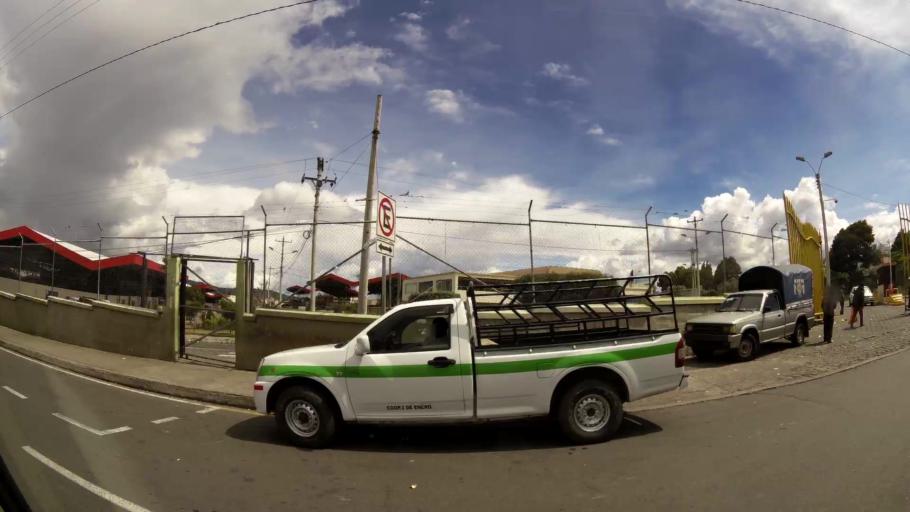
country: EC
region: Tungurahua
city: Ambato
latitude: -1.2698
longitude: -78.6165
